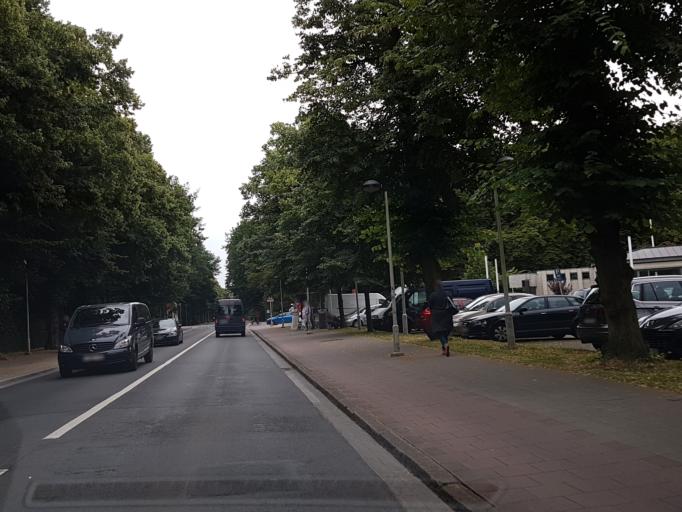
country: BE
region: Flanders
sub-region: Provincie Antwerpen
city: Borsbeek
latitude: 51.2189
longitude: 4.4605
